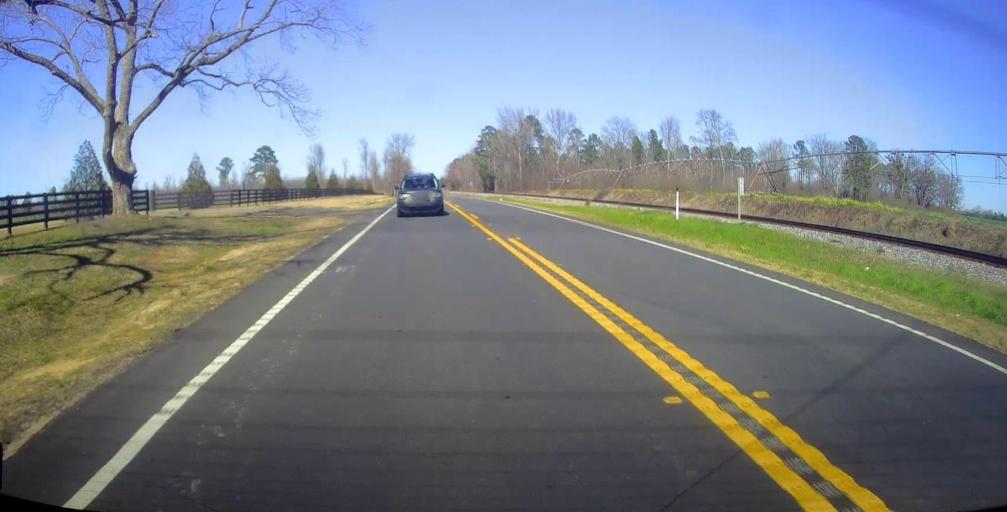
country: US
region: Georgia
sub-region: Macon County
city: Marshallville
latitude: 32.4766
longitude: -83.9337
